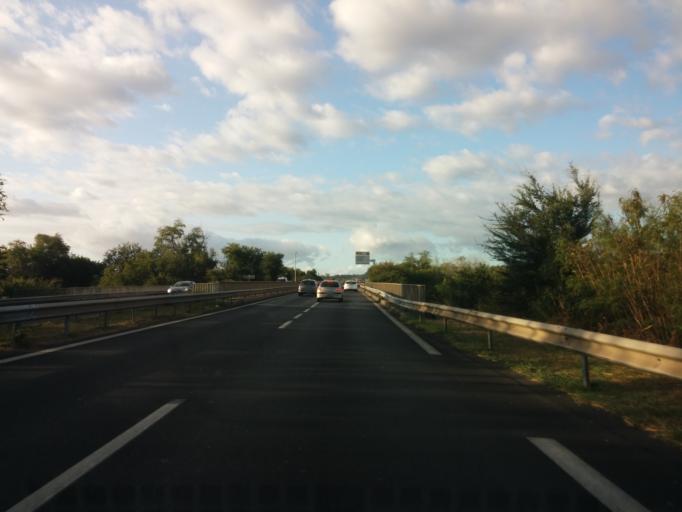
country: RE
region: Reunion
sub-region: Reunion
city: Saint-Paul
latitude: -20.9908
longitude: 55.2891
